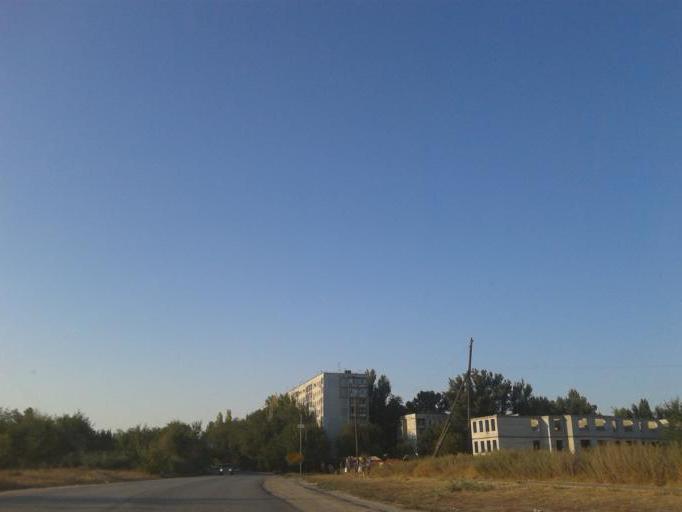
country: RU
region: Volgograd
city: Volgograd
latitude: 48.7633
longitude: 44.4976
